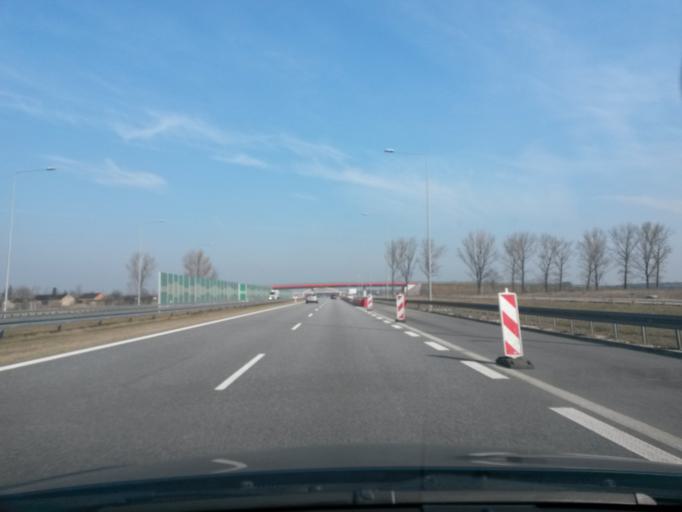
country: PL
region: Lodz Voivodeship
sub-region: Powiat kutnowski
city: Krzyzanow
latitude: 52.1791
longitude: 19.4867
